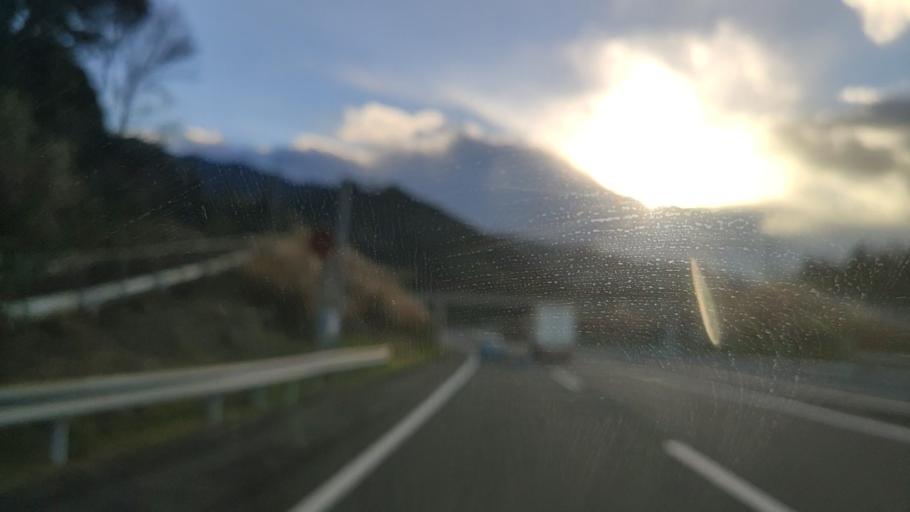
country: JP
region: Ehime
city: Saijo
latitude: 33.8689
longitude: 133.0596
